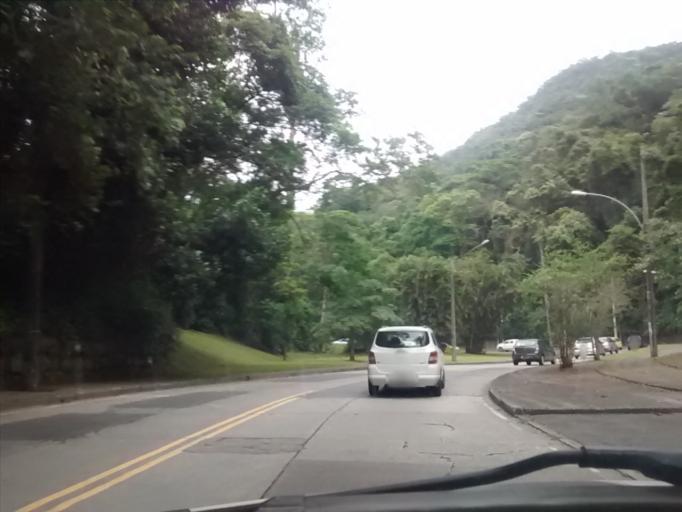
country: BR
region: Rio de Janeiro
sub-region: Rio De Janeiro
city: Rio de Janeiro
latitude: -22.9569
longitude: -43.2678
